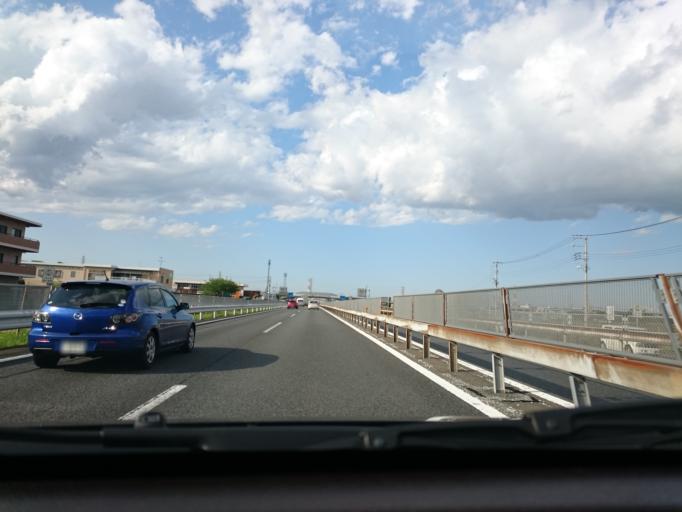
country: JP
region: Kanagawa
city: Isehara
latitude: 35.3880
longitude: 139.3321
